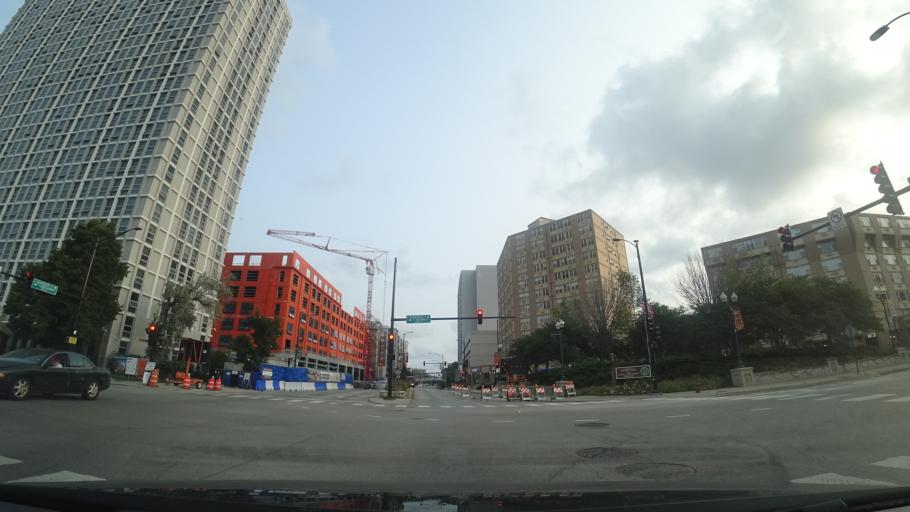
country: US
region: Illinois
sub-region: Cook County
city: Evanston
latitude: 41.9981
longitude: -87.6605
